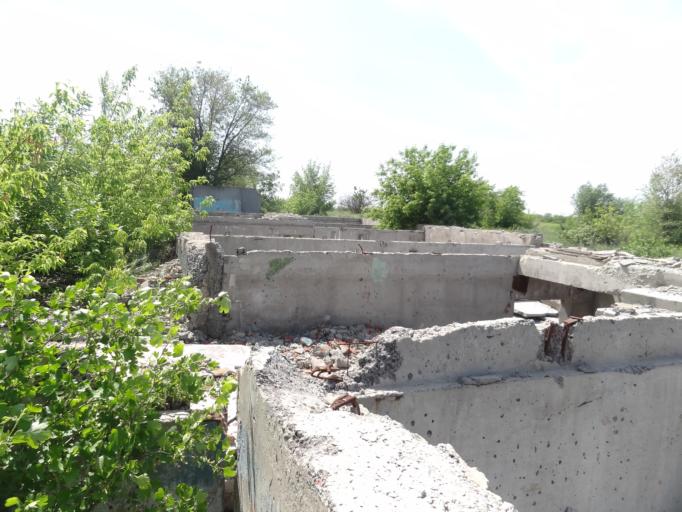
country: RU
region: Saratov
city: Engel's
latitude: 51.3568
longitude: 46.1949
